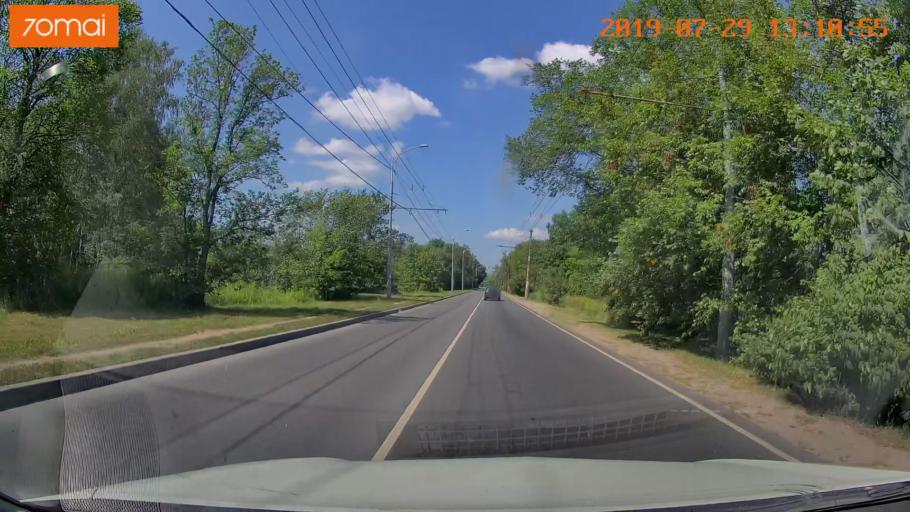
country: RU
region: Kaliningrad
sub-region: Gorod Kaliningrad
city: Kaliningrad
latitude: 54.7172
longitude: 20.3960
